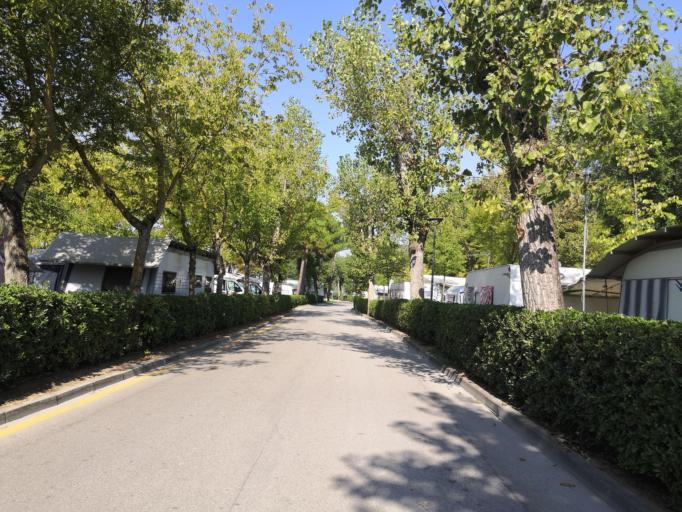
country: IT
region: Veneto
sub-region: Provincia di Venezia
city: Ca' Savio
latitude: 45.4348
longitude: 12.4395
